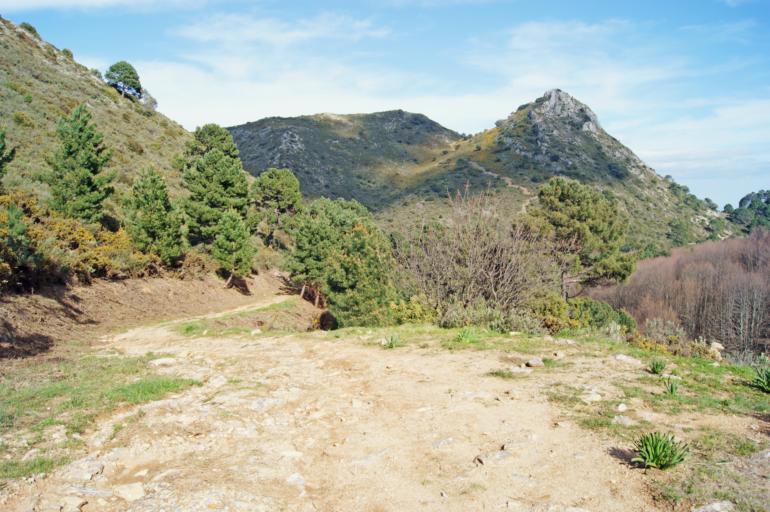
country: ES
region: Andalusia
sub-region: Provincia de Malaga
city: Ojen
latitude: 36.5815
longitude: -4.8905
